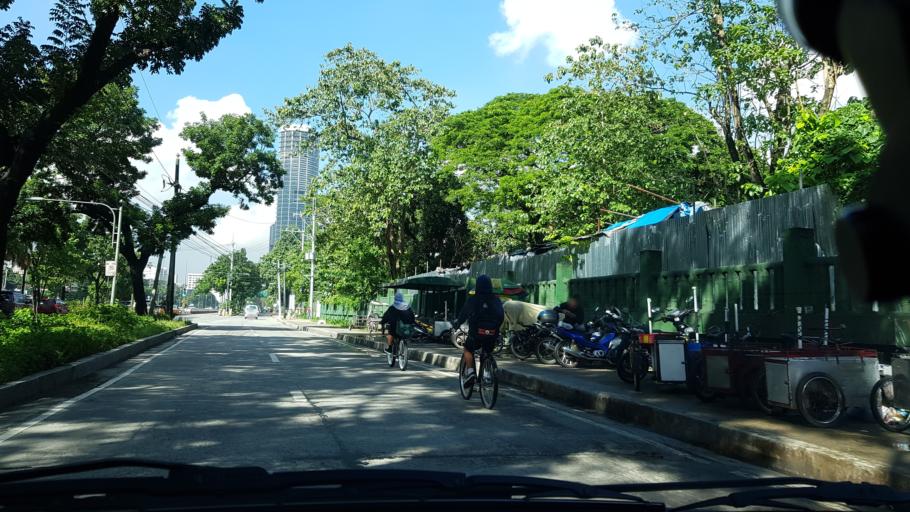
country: PH
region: Metro Manila
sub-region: Quezon City
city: Quezon City
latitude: 14.6481
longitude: 121.0436
